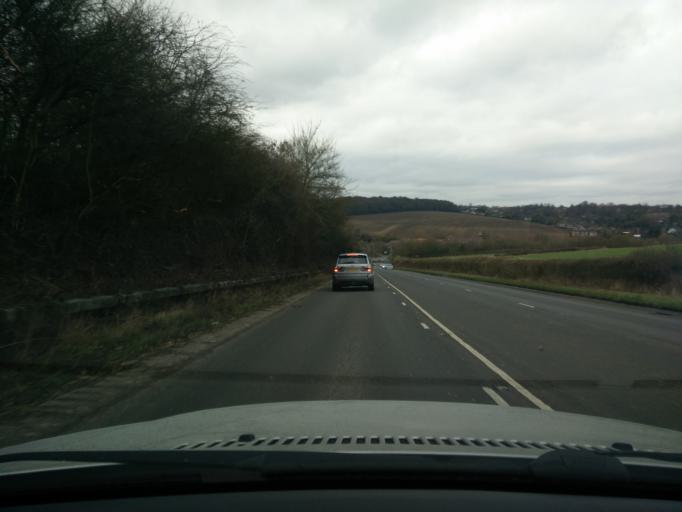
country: GB
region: England
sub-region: Buckinghamshire
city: Amersham
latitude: 51.6604
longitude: -0.6137
